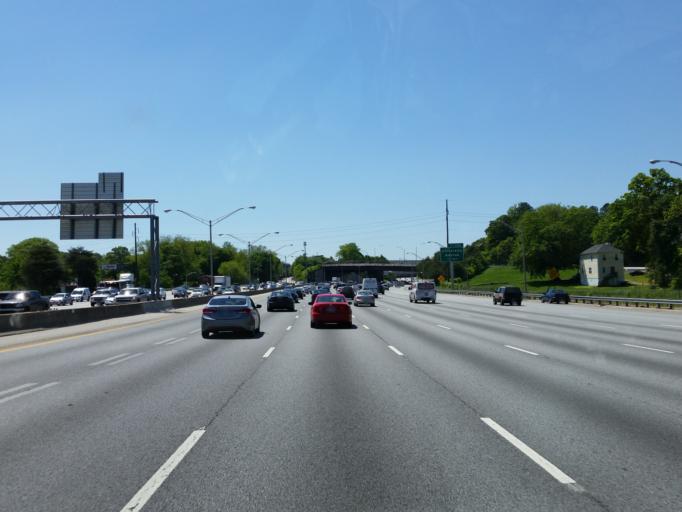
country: US
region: Georgia
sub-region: Fulton County
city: Atlanta
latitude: 33.7337
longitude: -84.3922
